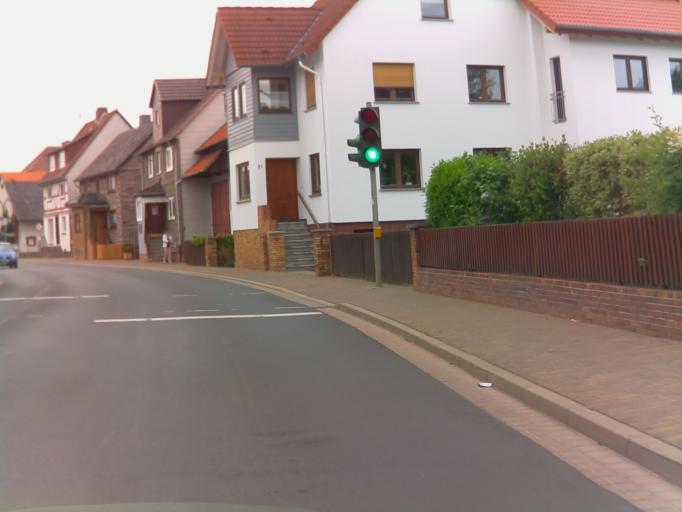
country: DE
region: Hesse
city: Schwalmstadt
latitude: 50.8856
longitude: 9.2520
